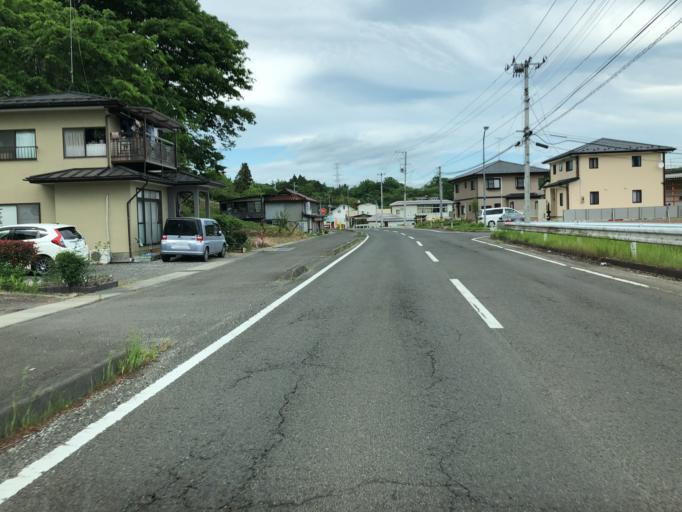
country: JP
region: Fukushima
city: Nihommatsu
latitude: 37.6384
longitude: 140.4991
